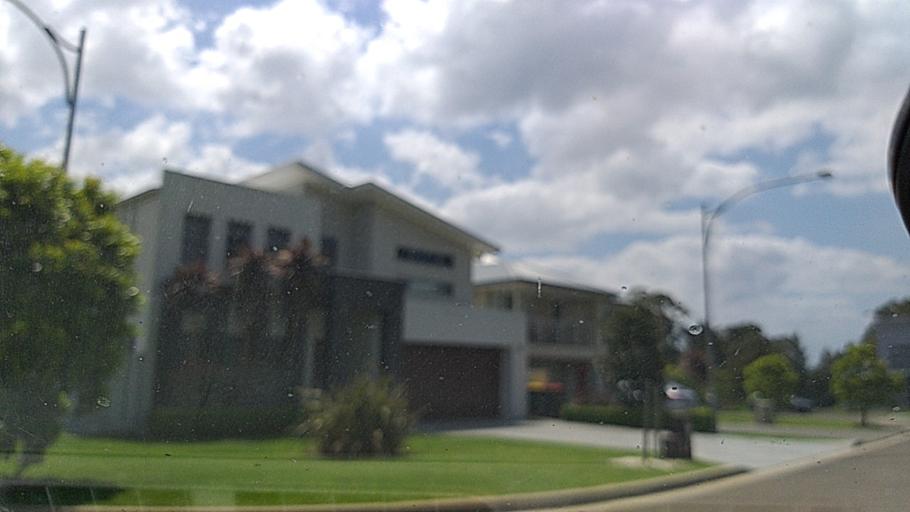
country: AU
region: New South Wales
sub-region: Wollongong
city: Bulli
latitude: -34.3281
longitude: 150.9173
